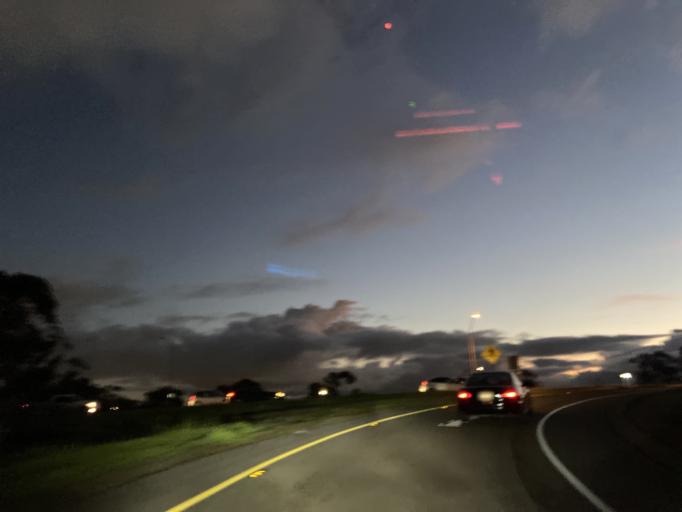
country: US
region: California
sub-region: San Diego County
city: La Jolla
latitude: 32.8339
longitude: -117.1684
